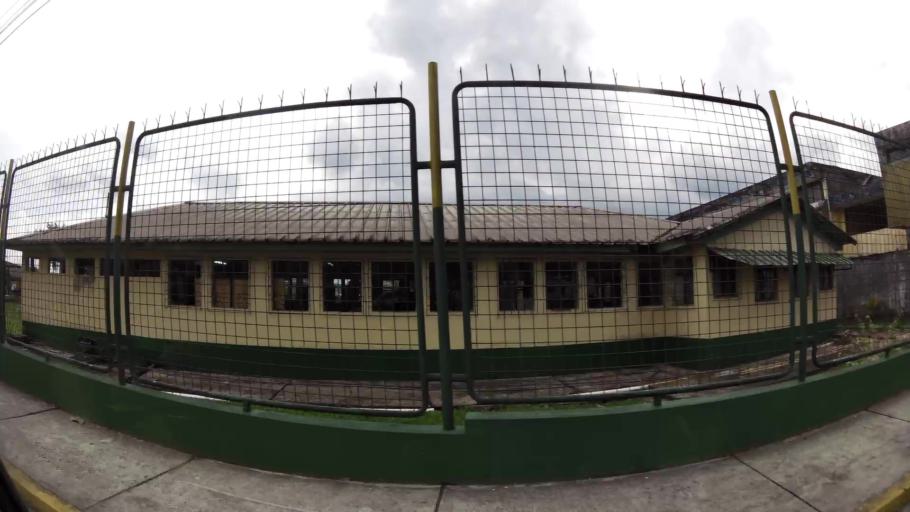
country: EC
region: Pastaza
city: Puyo
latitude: -1.5041
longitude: -78.0617
